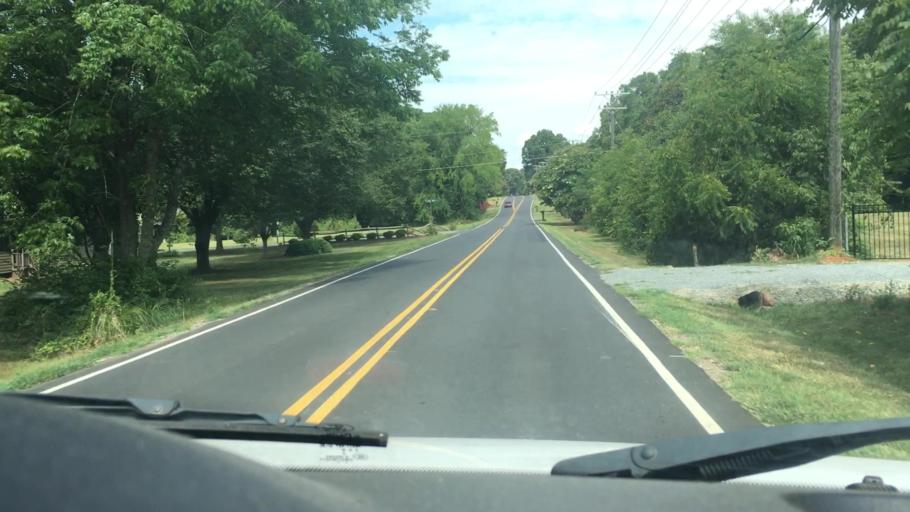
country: US
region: North Carolina
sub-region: Gaston County
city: Davidson
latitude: 35.5397
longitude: -80.8368
